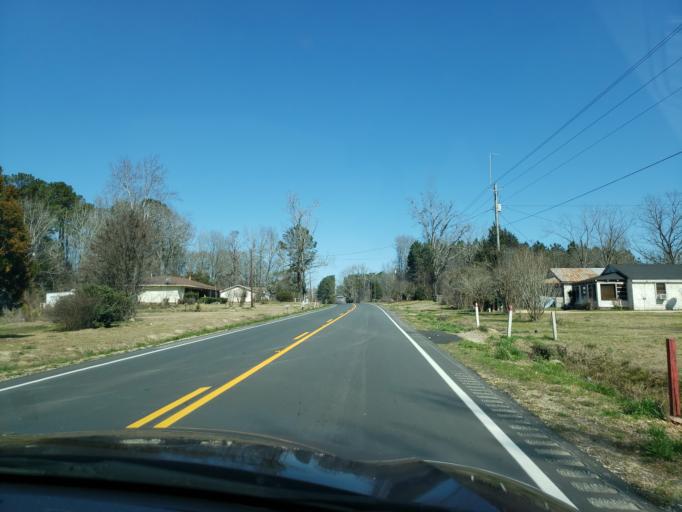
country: US
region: Alabama
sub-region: Macon County
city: Tuskegee
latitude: 32.5660
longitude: -85.6657
